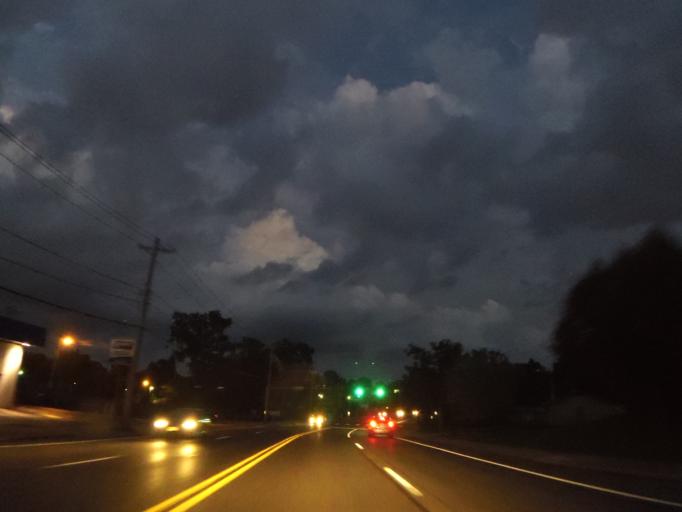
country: US
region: Missouri
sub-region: Saint Louis County
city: Saint George
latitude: 38.5286
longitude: -90.3026
